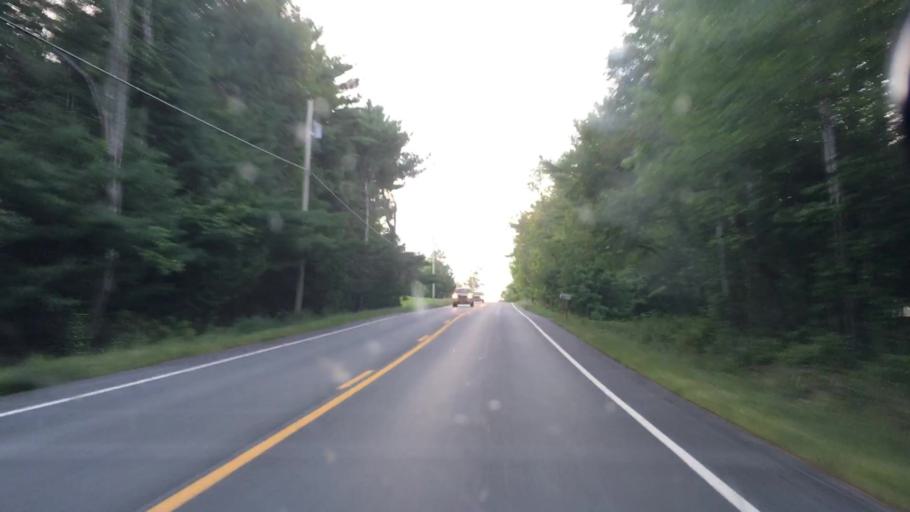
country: US
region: Maine
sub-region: Penobscot County
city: Hermon
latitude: 44.7517
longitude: -68.9706
